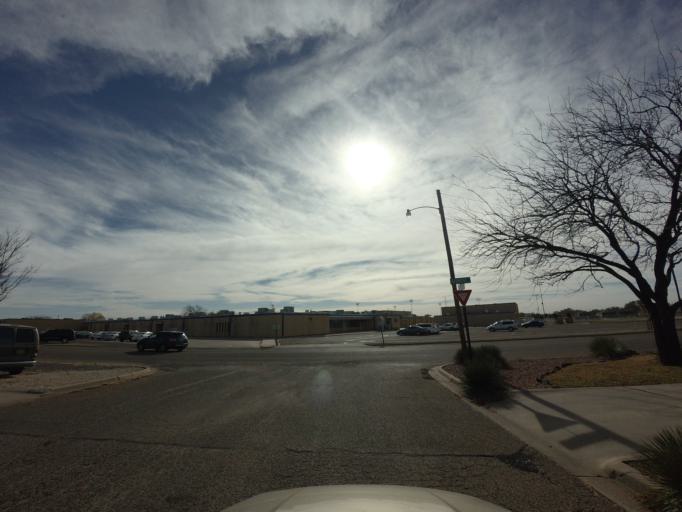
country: US
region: New Mexico
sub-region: Curry County
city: Clovis
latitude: 34.4151
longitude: -103.1901
